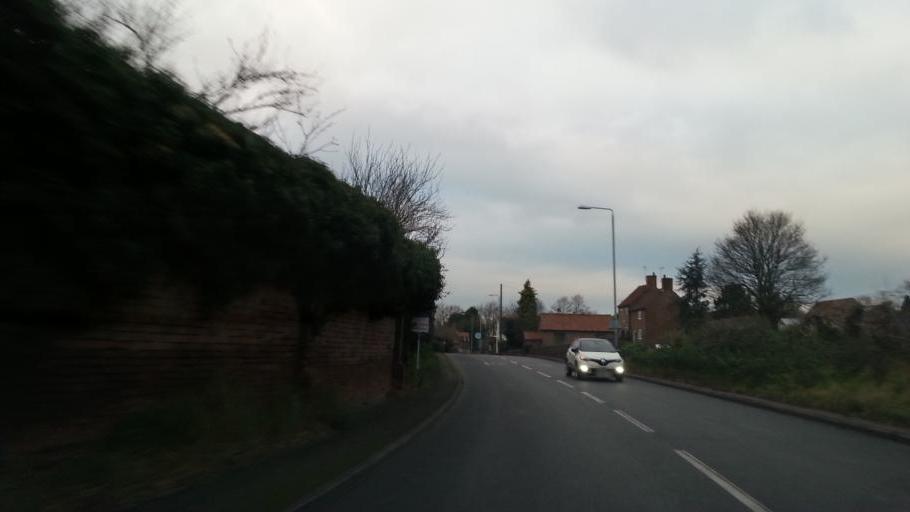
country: GB
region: England
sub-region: Nottinghamshire
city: Southwell
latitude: 53.1004
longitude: -0.9307
